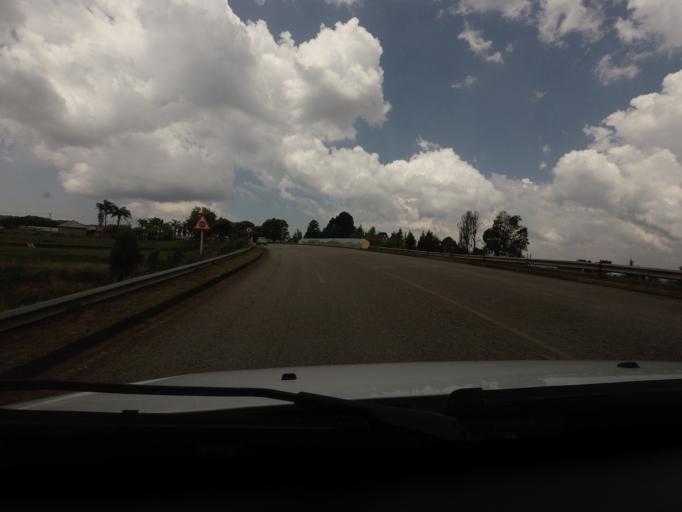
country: ZA
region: Mpumalanga
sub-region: Ehlanzeni District
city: Graksop
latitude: -24.9332
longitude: 30.8382
